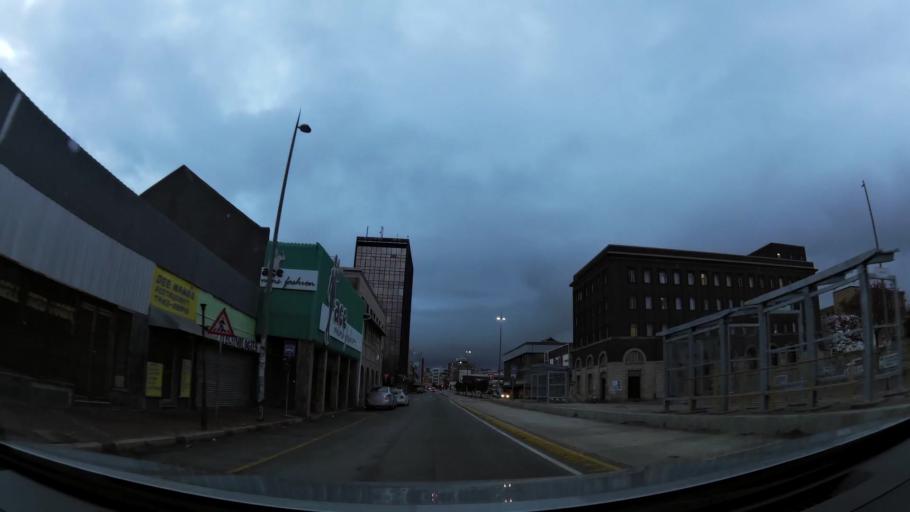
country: ZA
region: Eastern Cape
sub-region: Nelson Mandela Bay Metropolitan Municipality
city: Port Elizabeth
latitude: -33.9442
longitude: 25.6061
